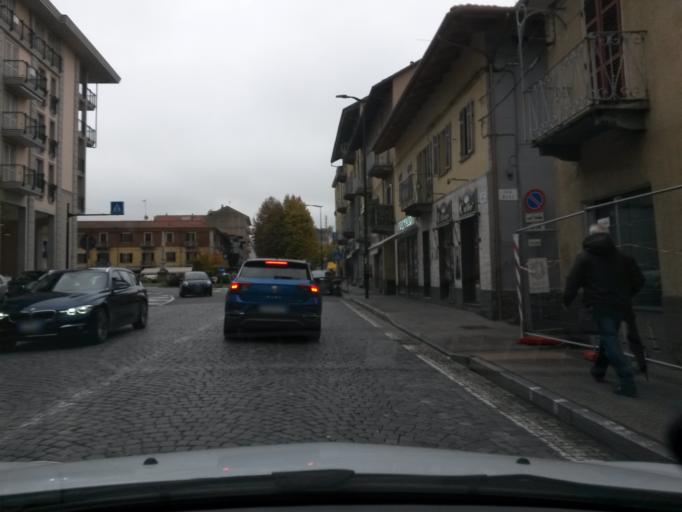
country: IT
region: Piedmont
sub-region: Provincia di Torino
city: Rivoli
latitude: 45.0711
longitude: 7.5198
